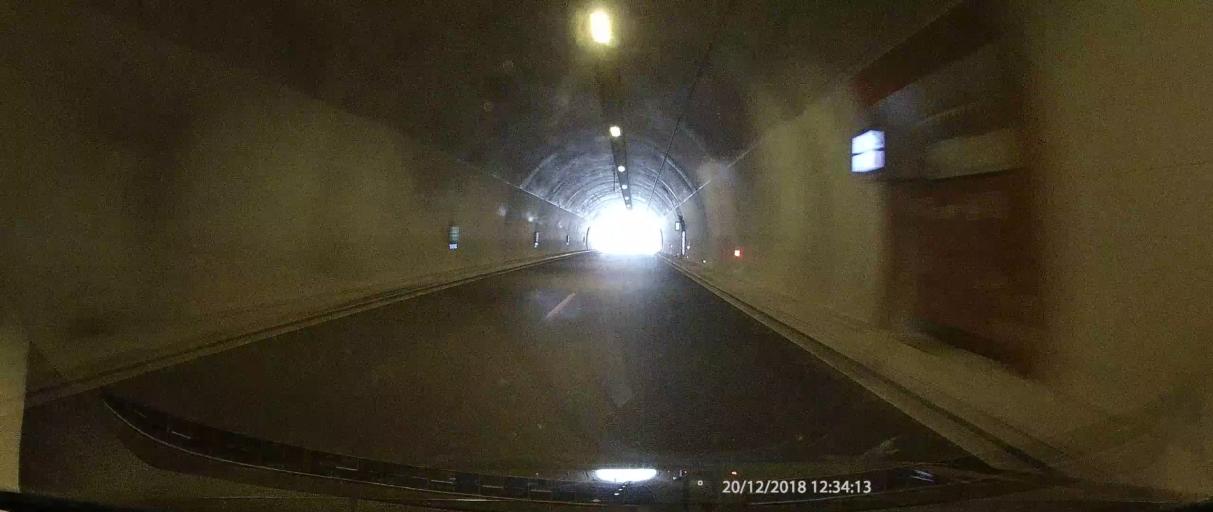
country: GR
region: West Greece
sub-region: Nomos Aitolias kai Akarnanias
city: Antirrio
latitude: 38.3534
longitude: 21.7217
